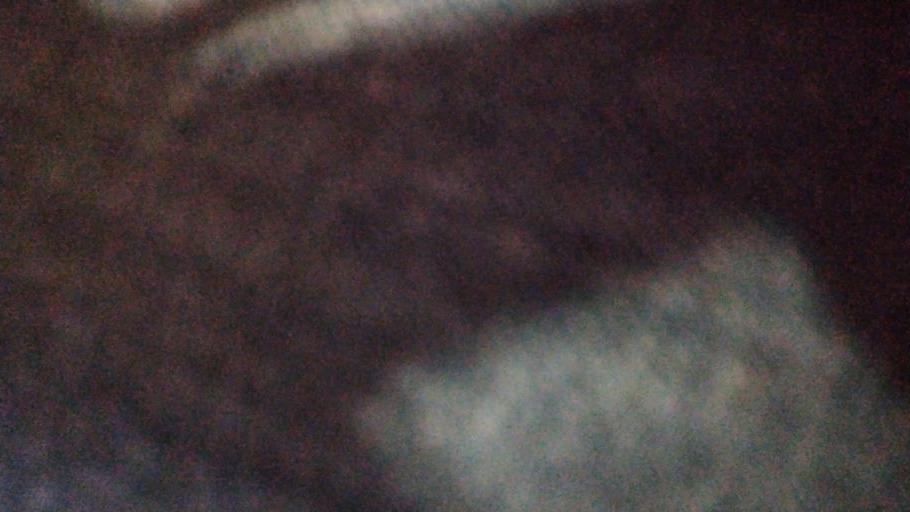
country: TW
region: Taiwan
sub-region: Changhua
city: Chang-hua
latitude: 24.0872
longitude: 120.5385
